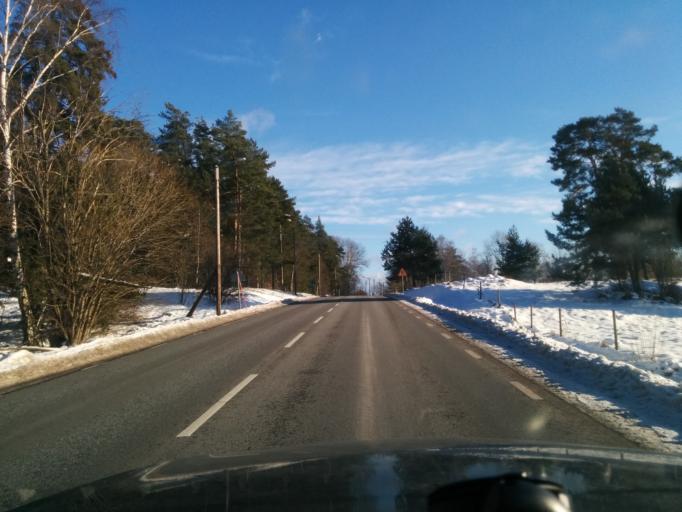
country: SE
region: Stockholm
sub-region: Taby Kommun
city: Taby
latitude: 59.4899
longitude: 18.0656
